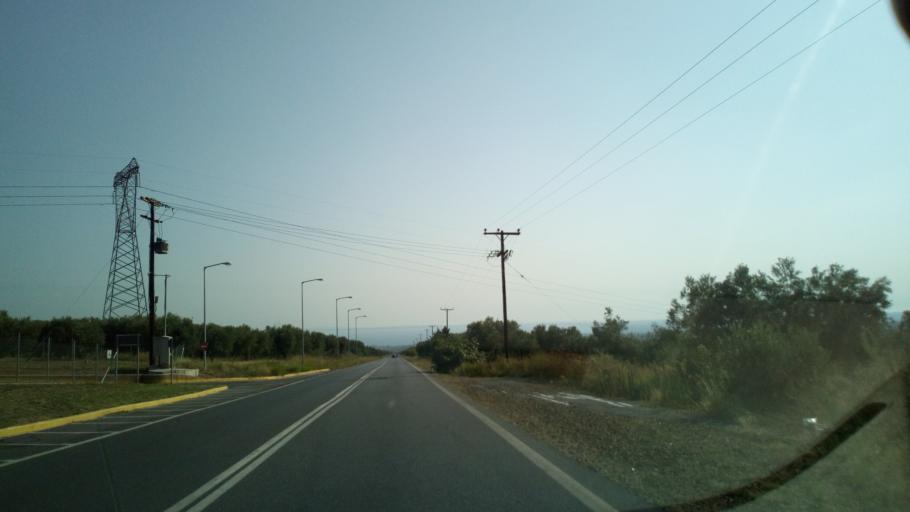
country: GR
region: Central Macedonia
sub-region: Nomos Chalkidikis
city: Kalyves Polygyrou
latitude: 40.3133
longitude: 23.4422
